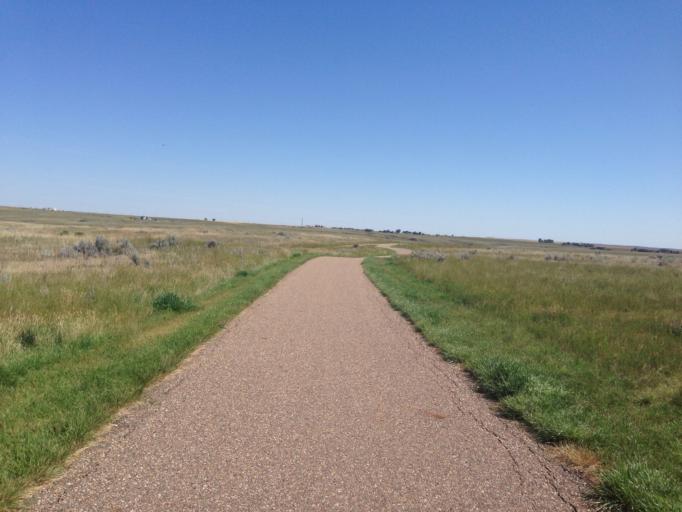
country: CA
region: Alberta
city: Medicine Hat
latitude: 50.0145
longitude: -110.6285
